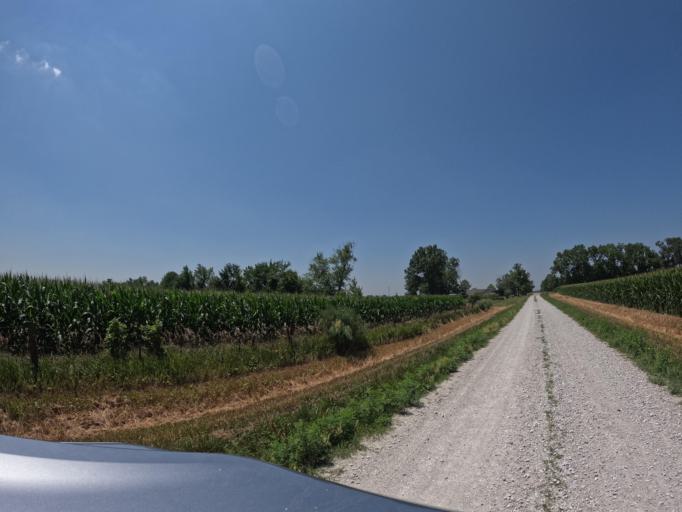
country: US
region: Iowa
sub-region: Keokuk County
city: Sigourney
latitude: 41.2748
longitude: -92.1635
